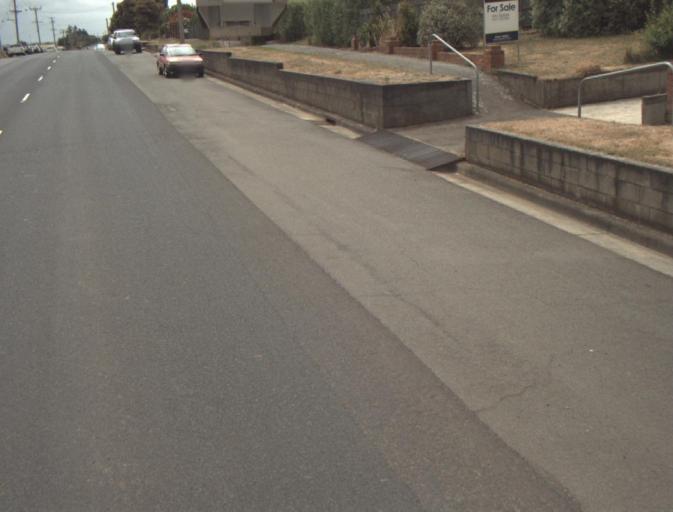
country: AU
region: Tasmania
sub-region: Launceston
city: Newstead
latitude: -41.4505
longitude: 147.1903
